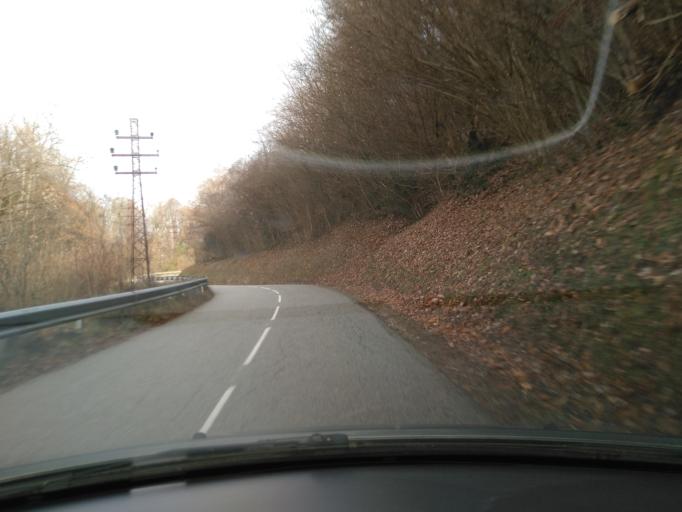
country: FR
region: Rhone-Alpes
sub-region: Departement de l'Isere
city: Villard-Bonnot
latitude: 45.2470
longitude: 5.9039
